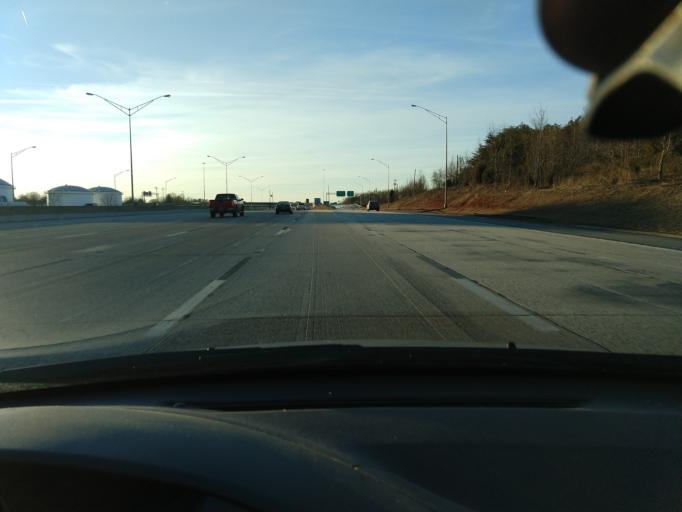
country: US
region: North Carolina
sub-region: Guilford County
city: Jamestown
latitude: 36.0740
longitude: -79.9380
